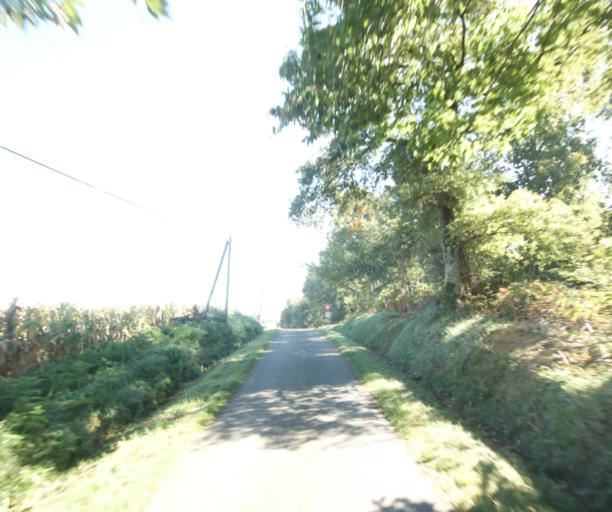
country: FR
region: Midi-Pyrenees
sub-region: Departement du Gers
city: Eauze
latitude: 43.8078
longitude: 0.1273
